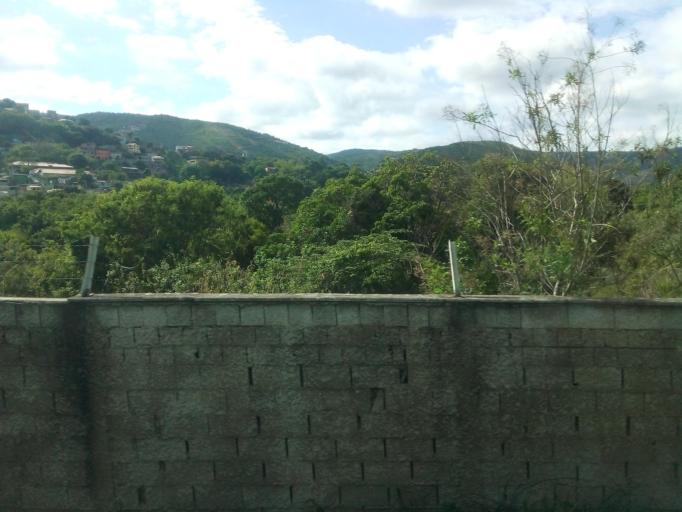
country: BR
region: Minas Gerais
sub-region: Belo Horizonte
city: Belo Horizonte
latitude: -19.8846
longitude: -43.8637
